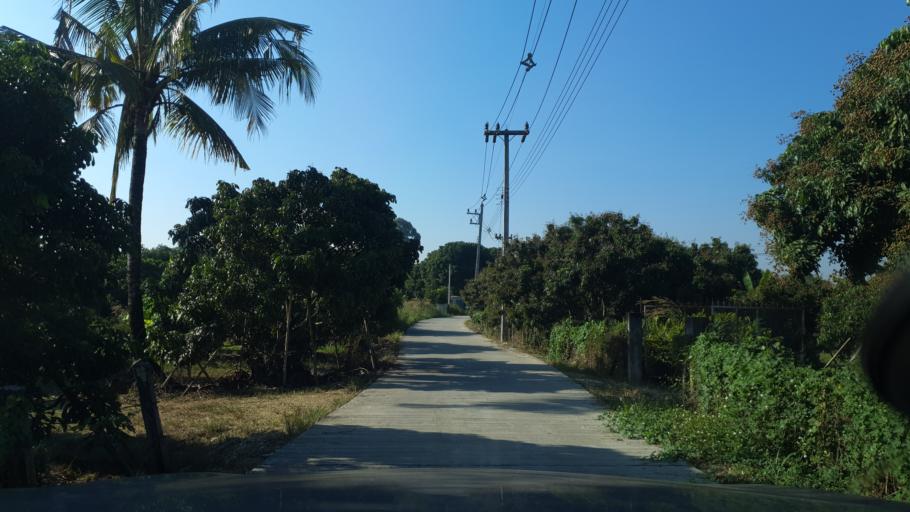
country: TH
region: Chiang Mai
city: San Kamphaeng
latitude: 18.6889
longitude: 99.1438
